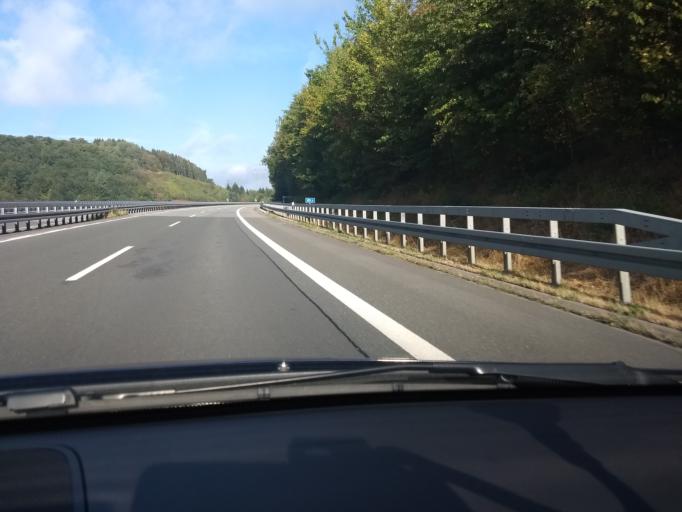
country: DE
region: North Rhine-Westphalia
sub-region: Regierungsbezirk Arnsberg
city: Meschede
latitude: 51.3593
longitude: 8.3335
